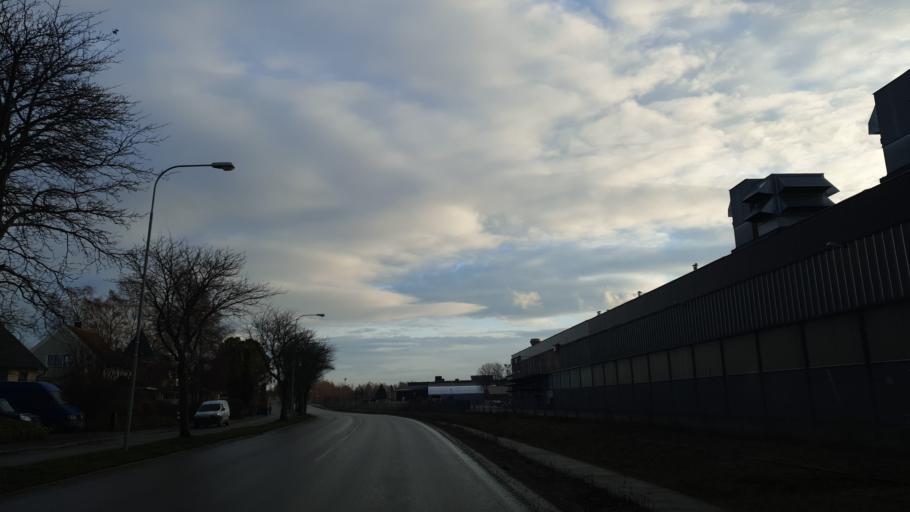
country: SE
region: Gaevleborg
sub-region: Hudiksvalls Kommun
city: Hudiksvall
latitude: 61.7249
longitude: 17.1307
